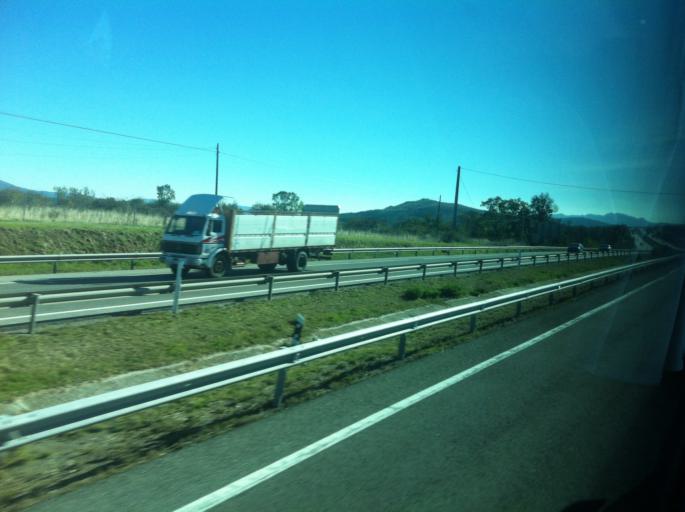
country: ES
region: Madrid
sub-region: Provincia de Madrid
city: Horcajo de la Sierra
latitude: 41.0543
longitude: -3.6143
